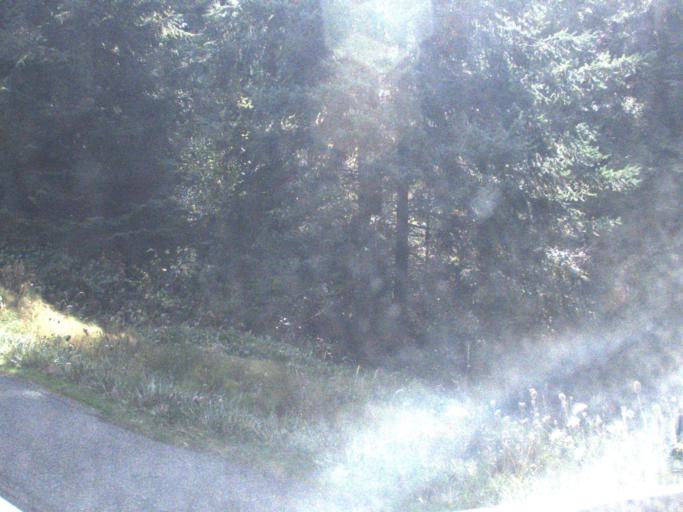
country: US
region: Washington
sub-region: Island County
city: Coupeville
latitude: 48.2214
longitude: -122.7347
